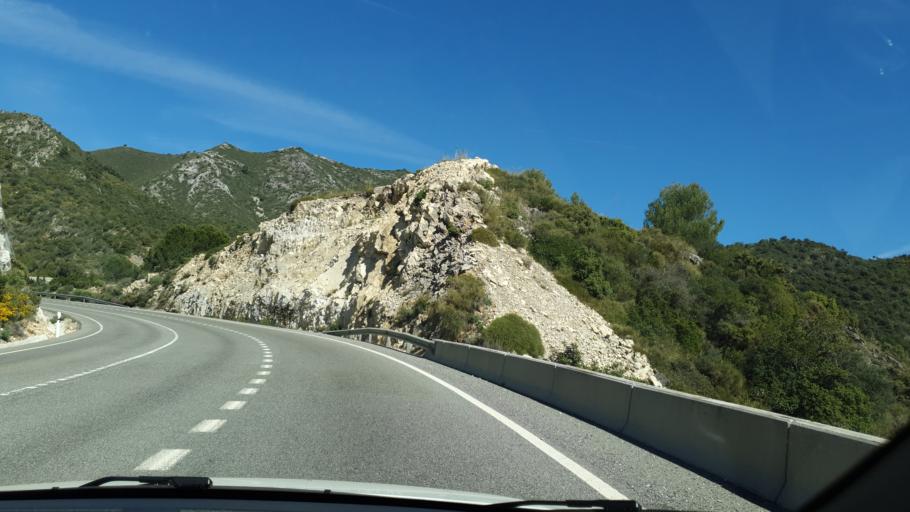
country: ES
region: Andalusia
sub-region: Provincia de Malaga
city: Ojen
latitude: 36.5650
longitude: -4.8616
